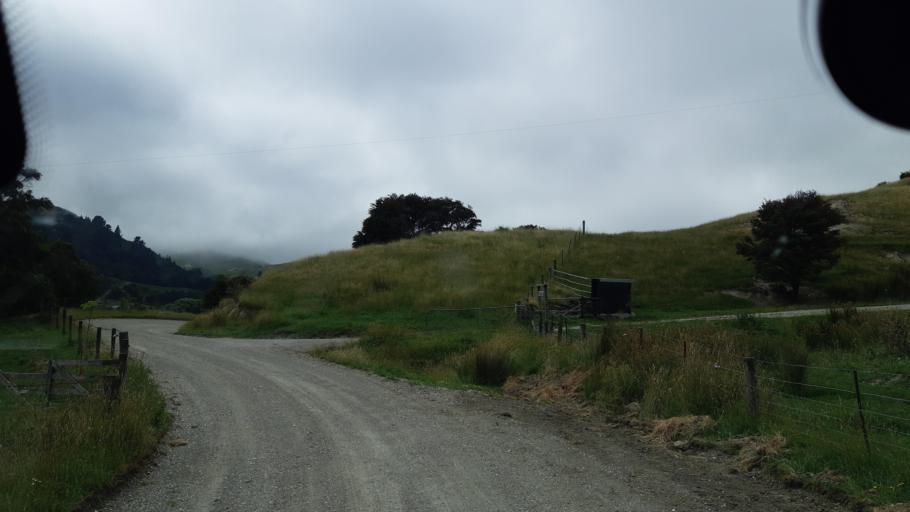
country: NZ
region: Marlborough
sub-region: Marlborough District
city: Blenheim
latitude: -41.9720
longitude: 173.9930
